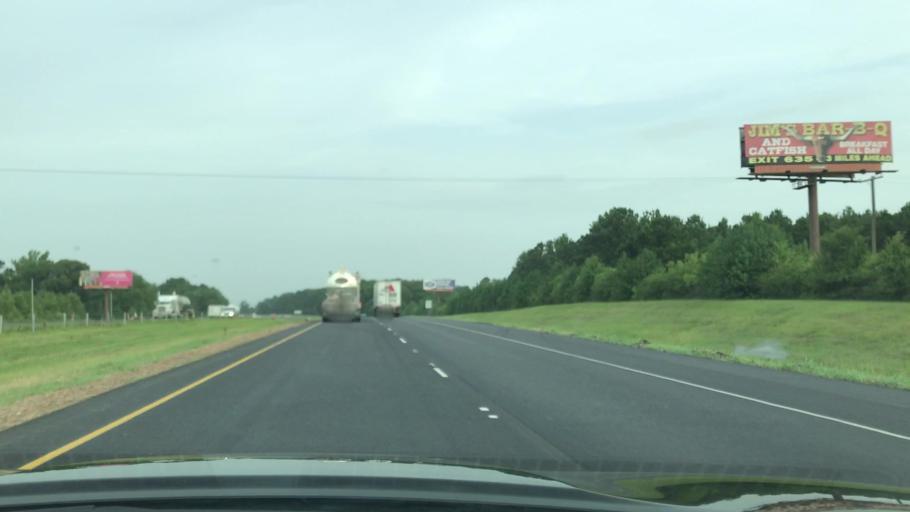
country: US
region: Louisiana
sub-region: Caddo Parish
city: Greenwood
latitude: 32.4496
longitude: -93.9895
